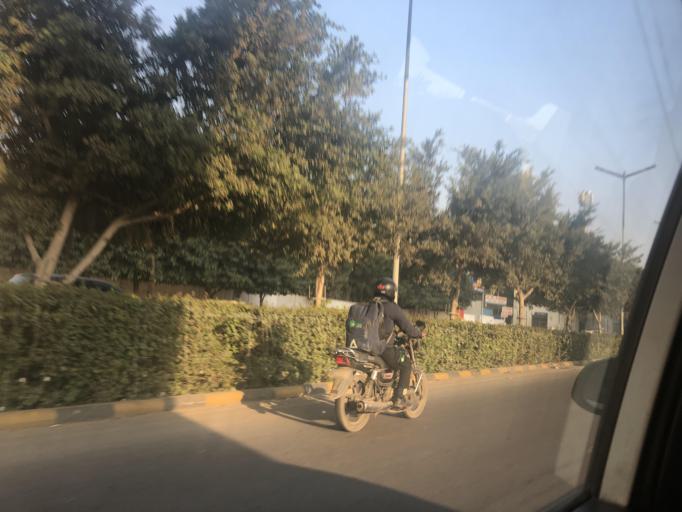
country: IN
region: Haryana
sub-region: Gurgaon
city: Gurgaon
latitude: 28.4883
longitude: 77.0919
